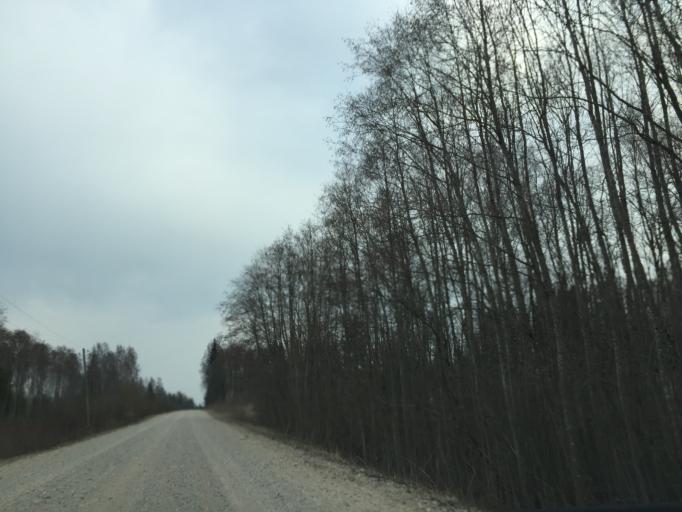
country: LV
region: Priekuli
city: Priekuli
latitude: 57.1754
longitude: 25.4863
